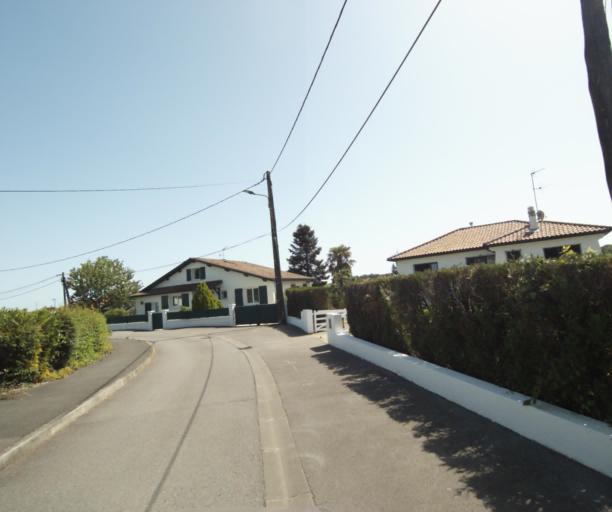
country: FR
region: Aquitaine
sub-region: Departement des Pyrenees-Atlantiques
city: Mouguerre
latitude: 43.4737
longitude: -1.4462
